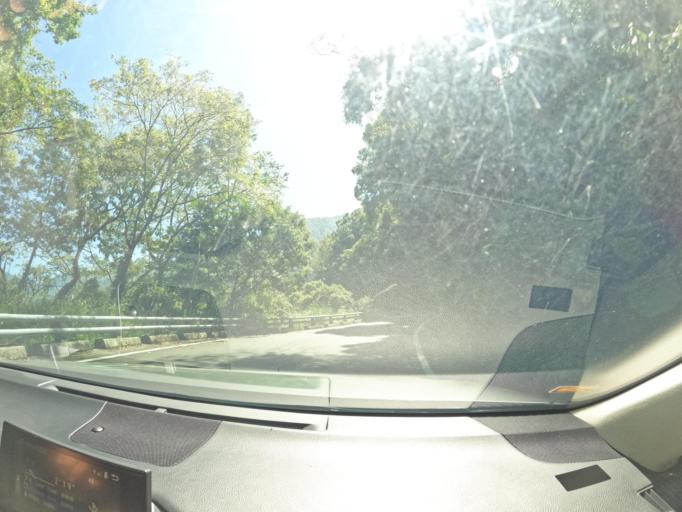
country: TW
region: Taiwan
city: Yujing
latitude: 23.2862
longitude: 120.8617
